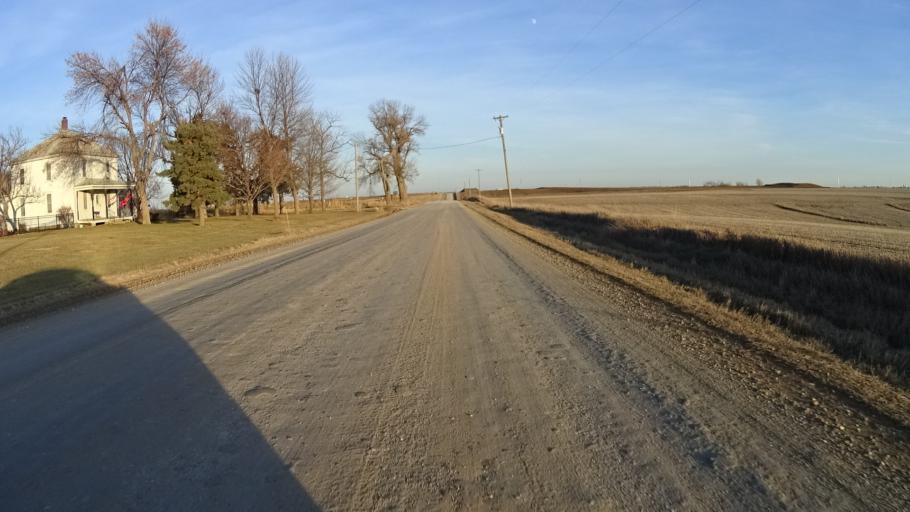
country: US
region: Nebraska
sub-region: Sarpy County
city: Springfield
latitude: 41.1326
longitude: -96.1045
